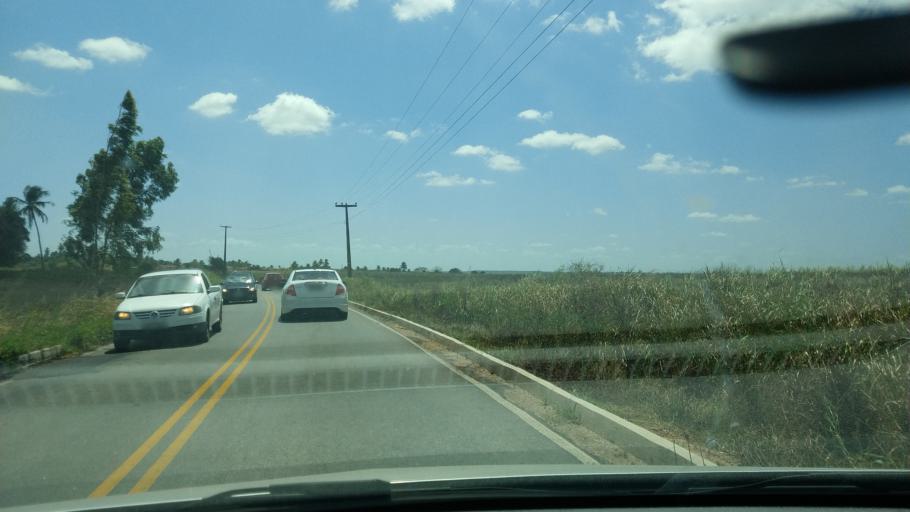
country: BR
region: Rio Grande do Norte
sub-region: Ares
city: Ares
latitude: -6.2377
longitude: -35.1741
